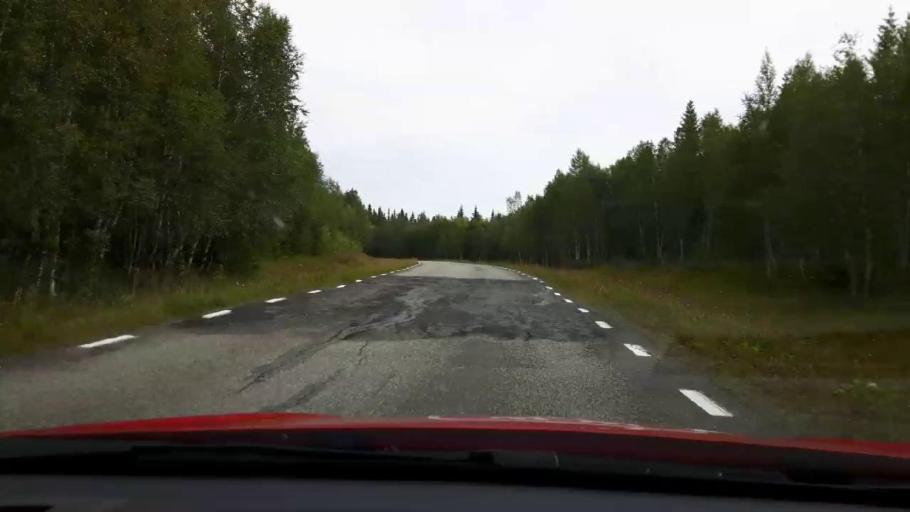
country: SE
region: Jaemtland
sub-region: Are Kommun
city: Are
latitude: 63.7372
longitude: 13.0257
